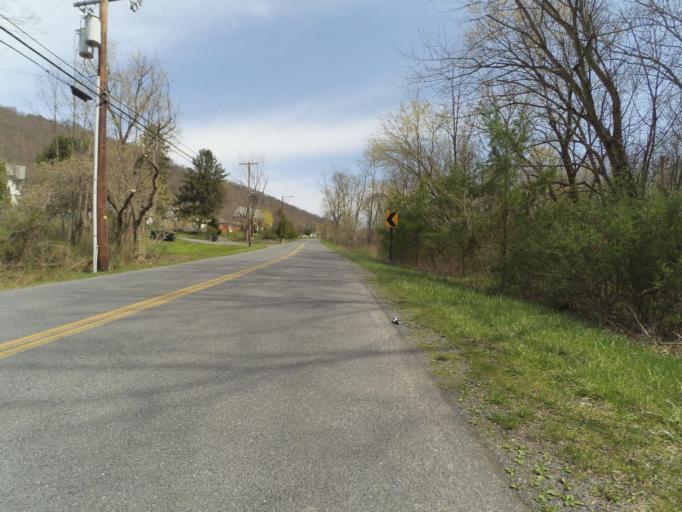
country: US
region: Pennsylvania
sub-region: Clinton County
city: Avis
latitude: 41.1760
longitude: -77.3500
